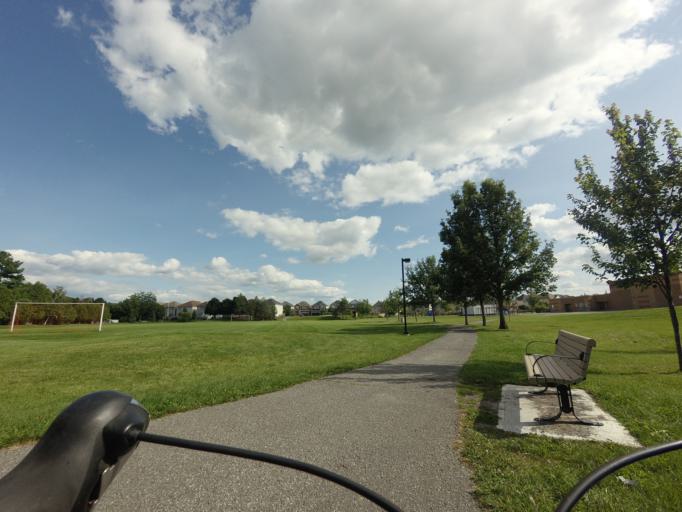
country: CA
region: Ontario
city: Bells Corners
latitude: 45.2883
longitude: -75.8457
